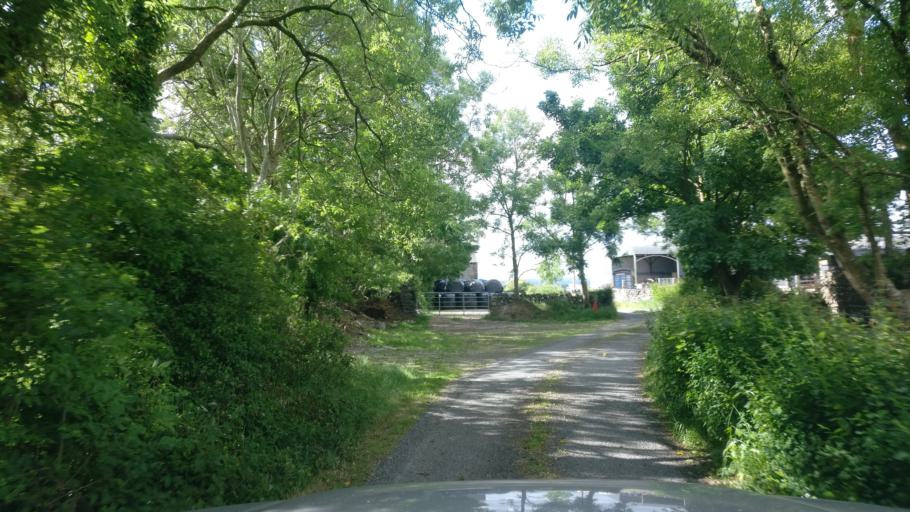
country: IE
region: Connaught
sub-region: County Galway
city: Loughrea
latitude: 53.2331
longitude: -8.6002
